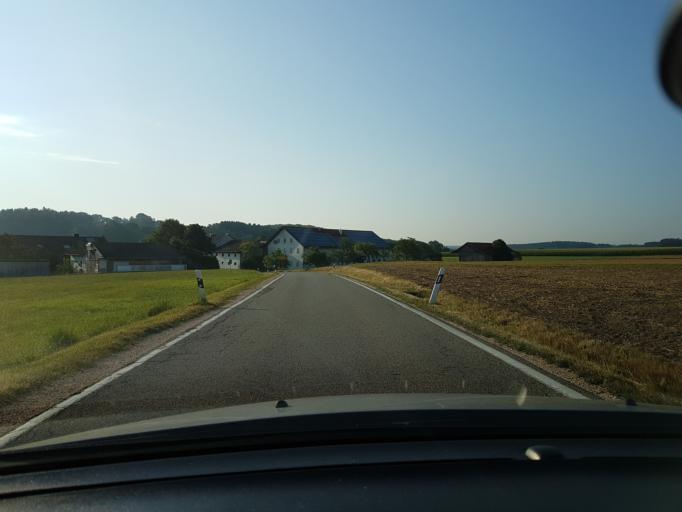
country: DE
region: Bavaria
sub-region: Upper Bavaria
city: Egglkofen
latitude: 48.4119
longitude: 12.4942
